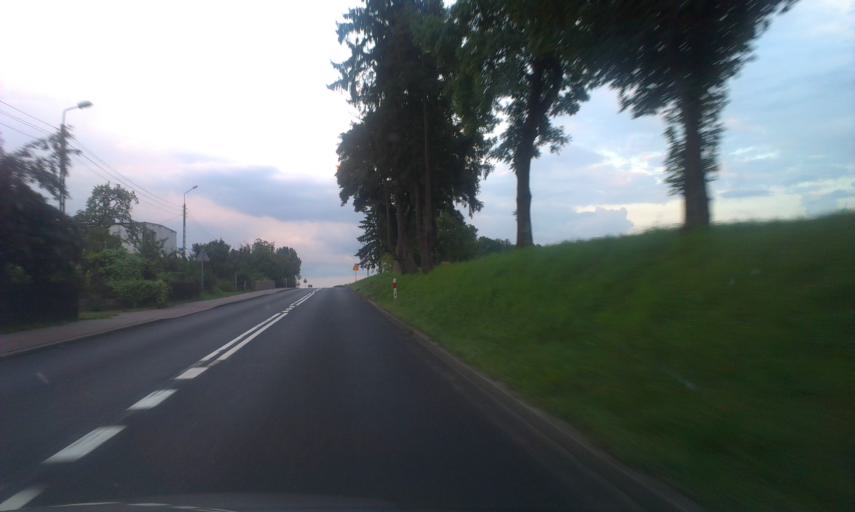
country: PL
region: West Pomeranian Voivodeship
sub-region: Powiat koszalinski
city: Bobolice
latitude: 54.0283
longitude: 16.4641
